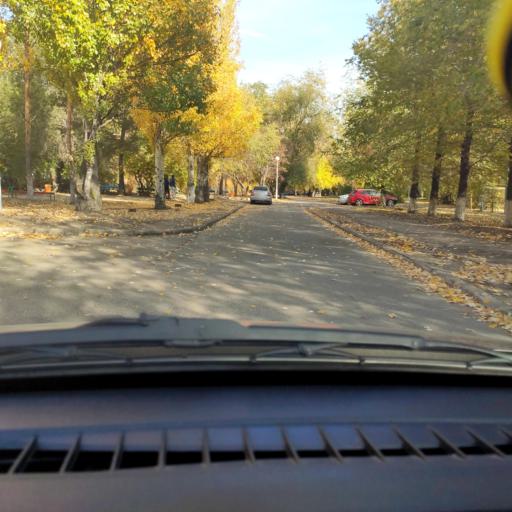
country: RU
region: Samara
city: Tol'yatti
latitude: 53.5334
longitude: 49.2929
